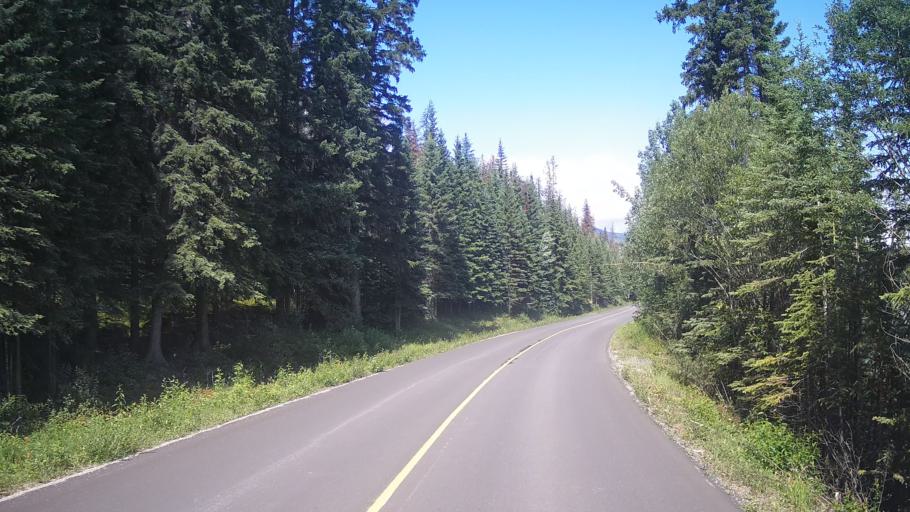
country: CA
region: Alberta
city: Jasper Park Lodge
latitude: 52.7419
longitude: -117.9656
